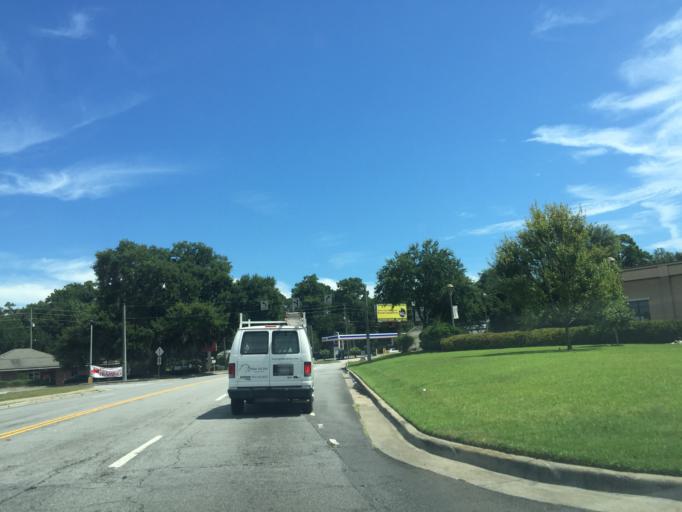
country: US
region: Georgia
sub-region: Chatham County
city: Isle of Hope
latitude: 32.0001
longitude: -81.1048
